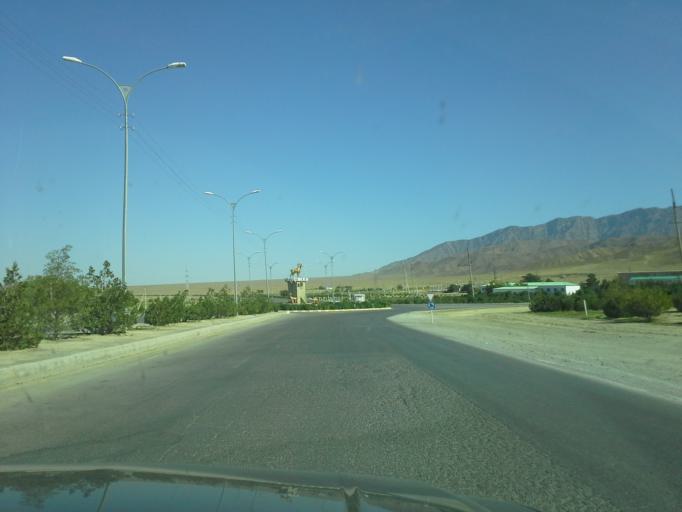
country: TM
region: Ahal
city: Baharly
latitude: 38.5198
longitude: 57.1849
